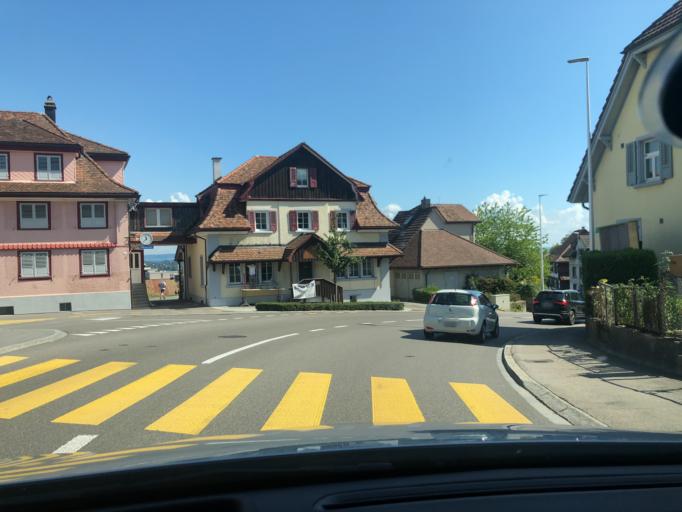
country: CH
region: Thurgau
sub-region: Kreuzlingen District
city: Kreuzlingen
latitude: 47.6424
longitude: 9.1685
